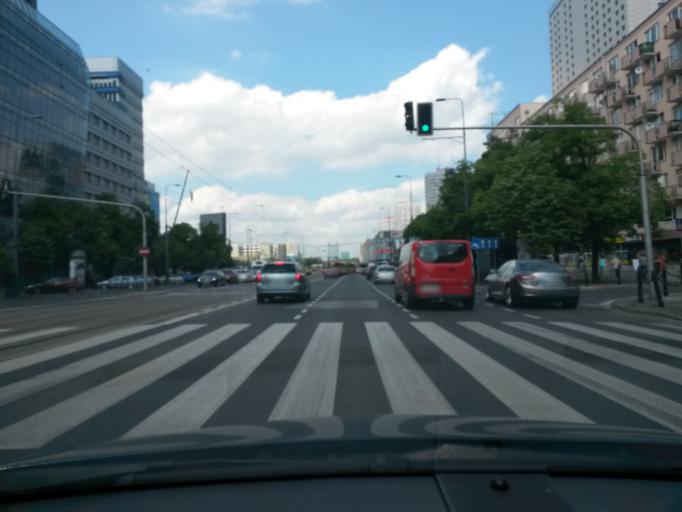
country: PL
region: Masovian Voivodeship
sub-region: Warszawa
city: Warsaw
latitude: 52.2278
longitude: 21.0131
